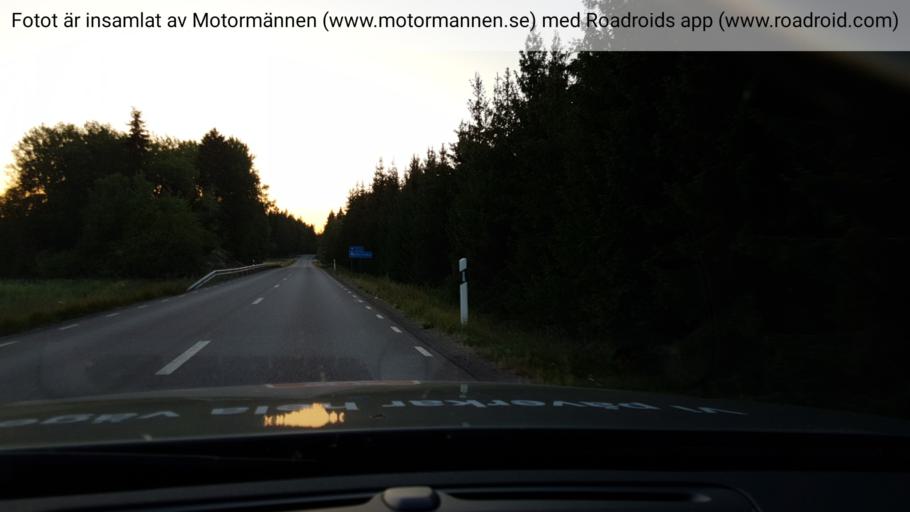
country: SE
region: Uppsala
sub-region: Heby Kommun
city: OEstervala
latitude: 59.9983
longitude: 17.3100
